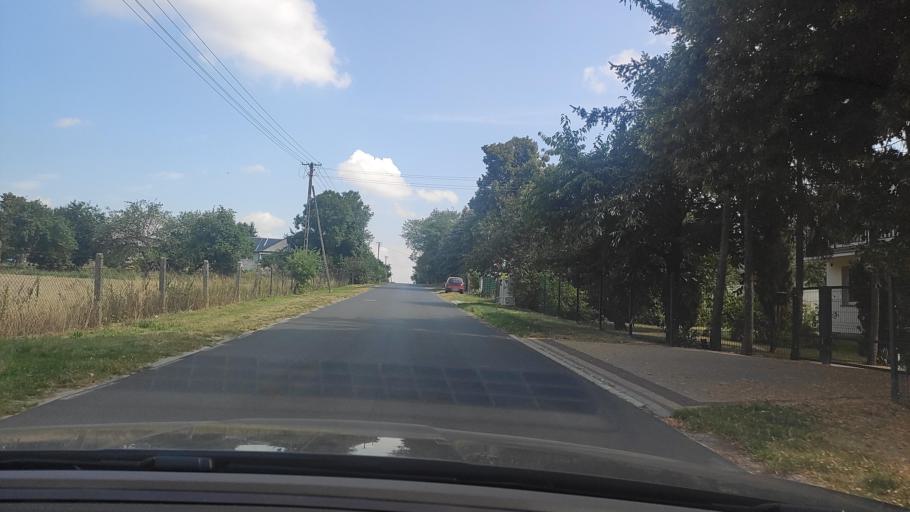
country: PL
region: Greater Poland Voivodeship
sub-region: Powiat poznanski
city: Kostrzyn
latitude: 52.4793
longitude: 17.1872
